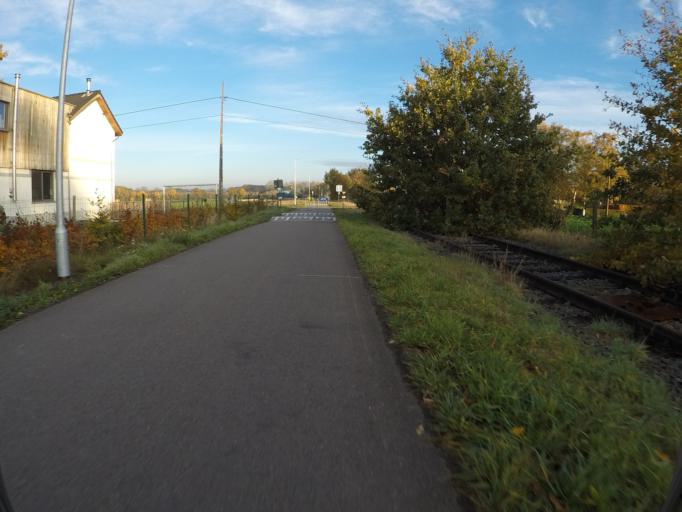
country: BE
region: Flanders
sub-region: Provincie Antwerpen
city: Olen
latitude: 51.1288
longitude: 4.8247
